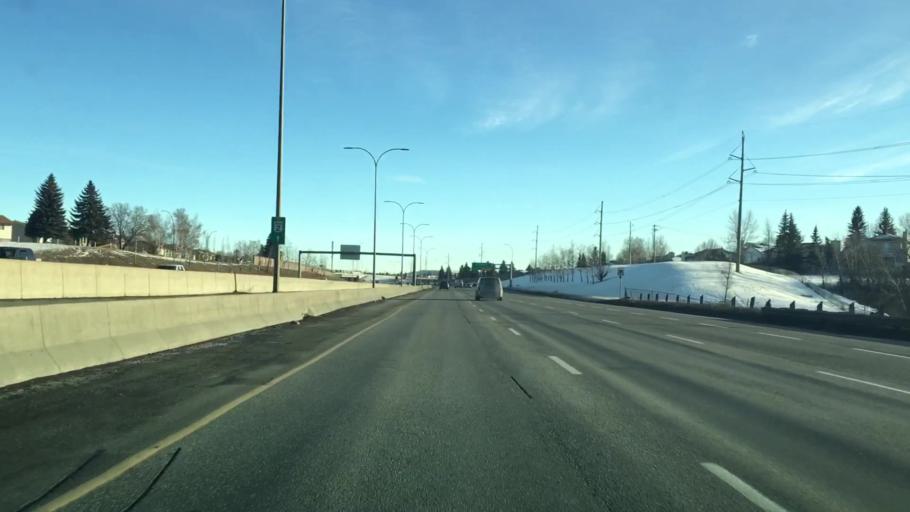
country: CA
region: Alberta
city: Calgary
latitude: 50.9856
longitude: -114.0236
